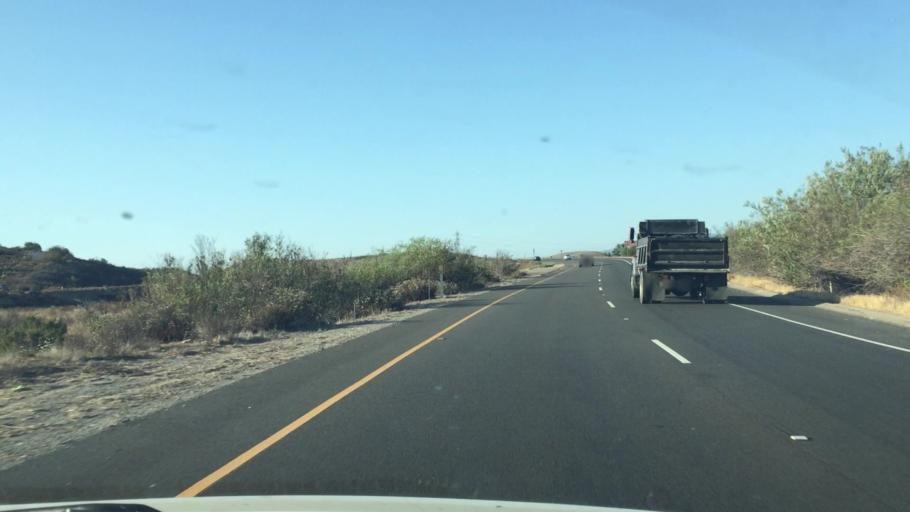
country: US
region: California
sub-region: Orange County
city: Laguna Woods
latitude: 33.6034
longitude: -117.7619
